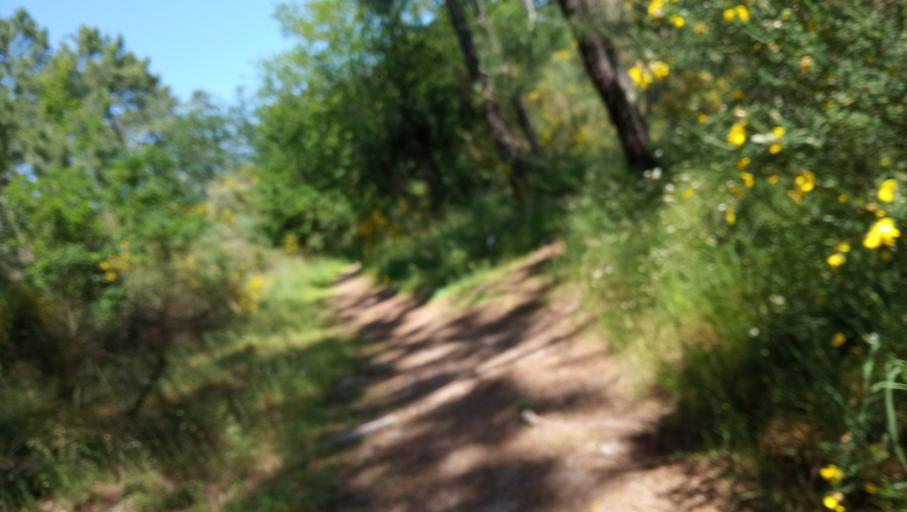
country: ES
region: Galicia
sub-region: Provincia de Pontevedra
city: A Guarda
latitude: 41.8750
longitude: -8.8656
